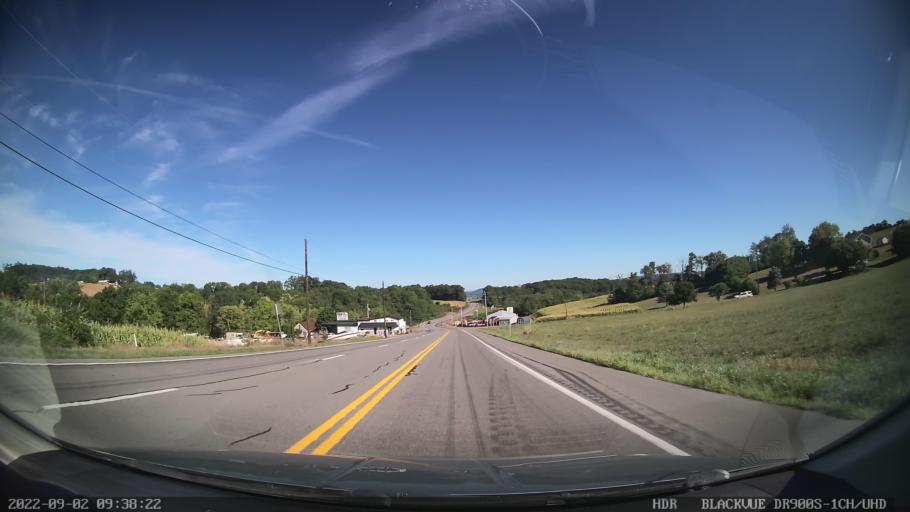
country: US
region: Pennsylvania
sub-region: Northumberland County
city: Elysburg
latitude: 40.8986
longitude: -76.5769
